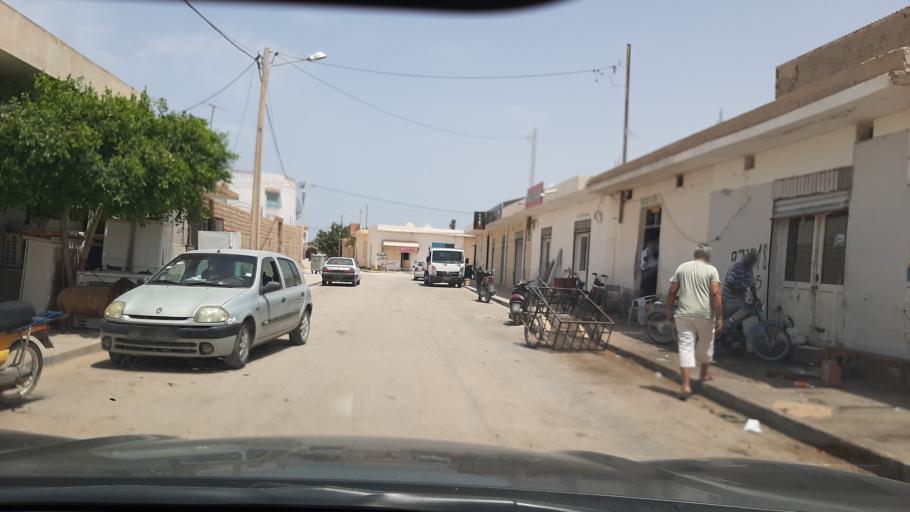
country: TN
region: Qabis
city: Gabes
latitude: 33.6180
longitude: 10.2911
